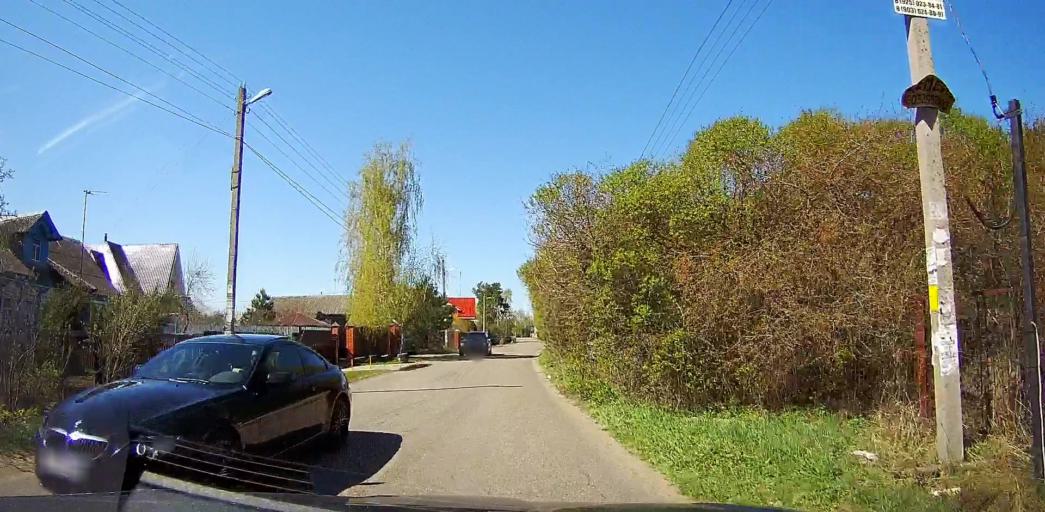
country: RU
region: Moskovskaya
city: Malyshevo
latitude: 55.4580
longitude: 38.3707
